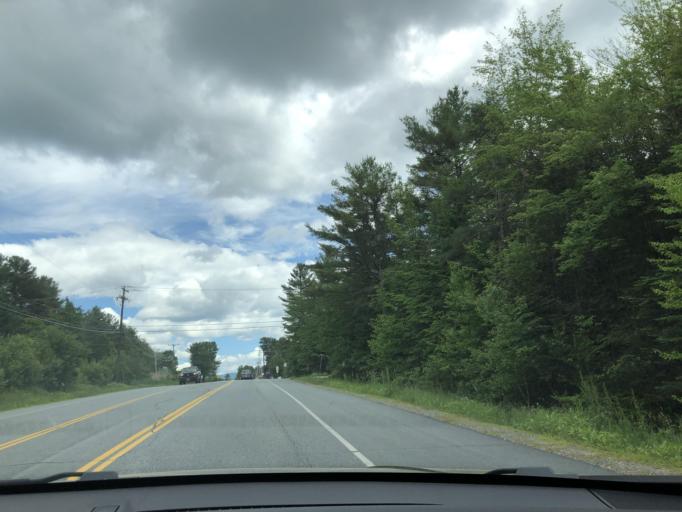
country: US
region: New Hampshire
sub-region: Merrimack County
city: New London
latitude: 43.4249
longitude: -72.0053
